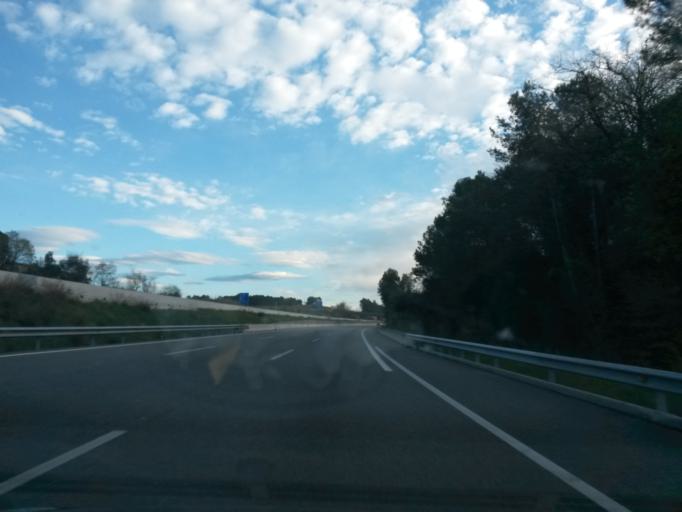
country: ES
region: Catalonia
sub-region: Provincia de Girona
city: Cervia de Ter
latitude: 42.0853
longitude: 2.8904
